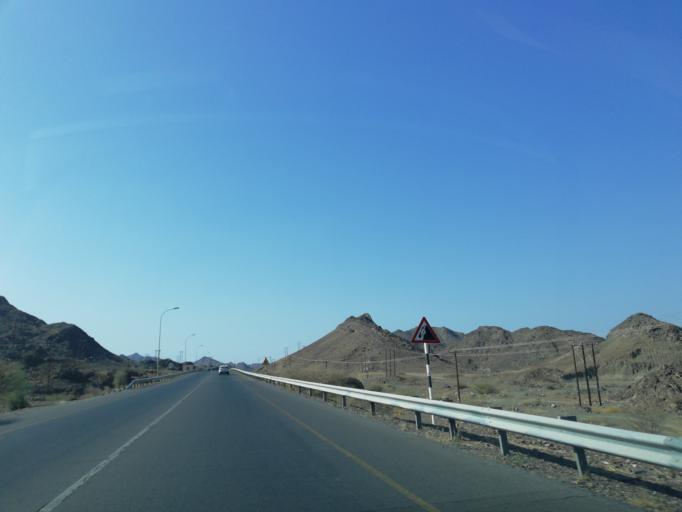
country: OM
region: Ash Sharqiyah
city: Ibra'
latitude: 22.8155
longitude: 58.1674
